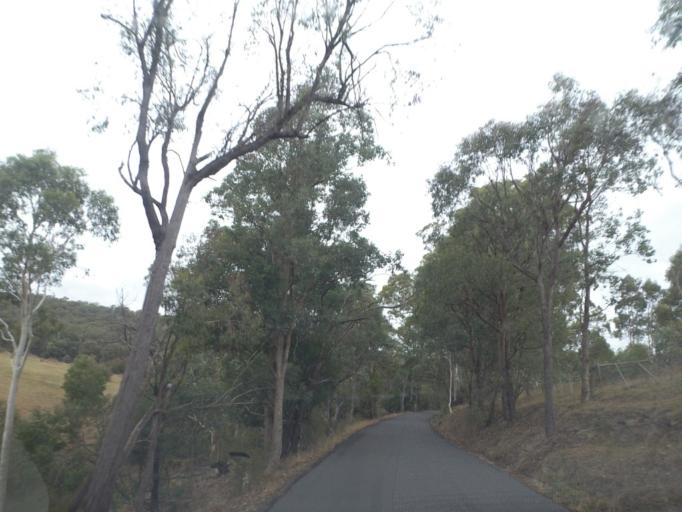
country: AU
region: Victoria
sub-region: Nillumbik
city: Saint Andrews
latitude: -37.6437
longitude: 145.2843
